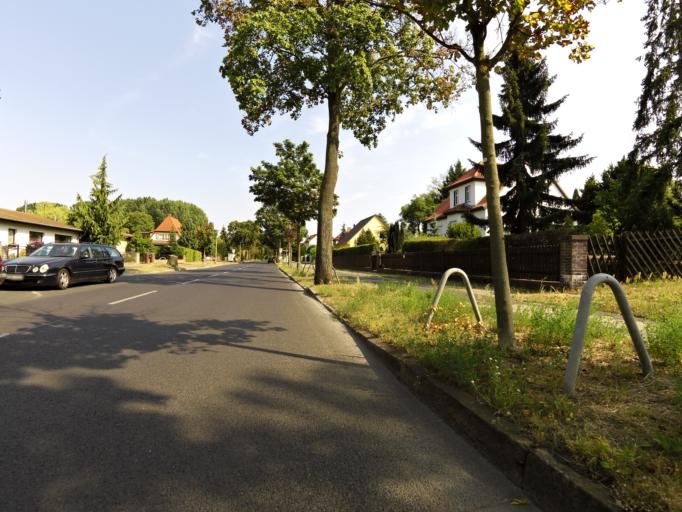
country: DE
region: Berlin
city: Altglienicke
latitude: 52.4178
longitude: 13.5521
